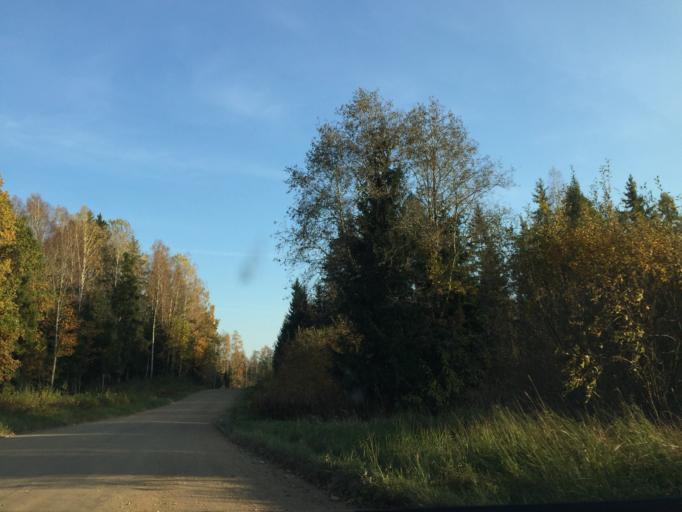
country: LV
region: Vainode
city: Vainode
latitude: 56.5954
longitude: 21.8328
